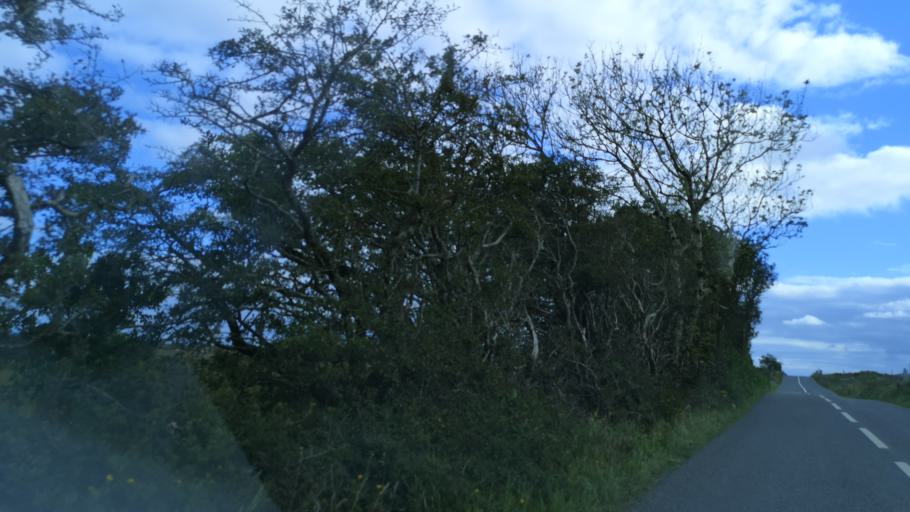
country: IE
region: Connaught
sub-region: County Galway
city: Bearna
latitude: 53.2865
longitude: -9.1635
